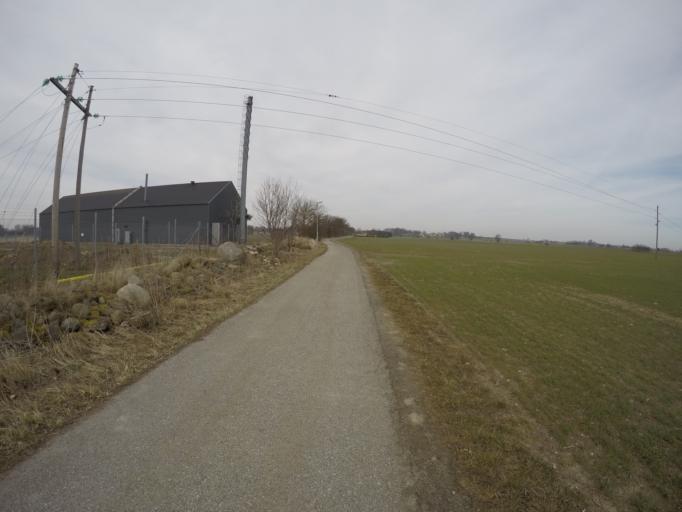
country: SE
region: Skane
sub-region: Ystads Kommun
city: Kopingebro
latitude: 55.4312
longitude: 14.1146
